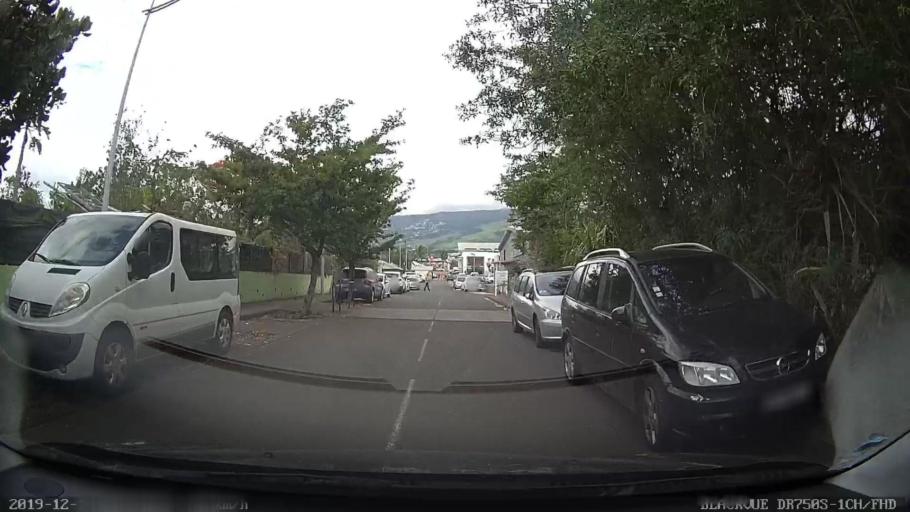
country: RE
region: Reunion
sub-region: Reunion
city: Sainte-Marie
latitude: -20.8983
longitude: 55.5041
